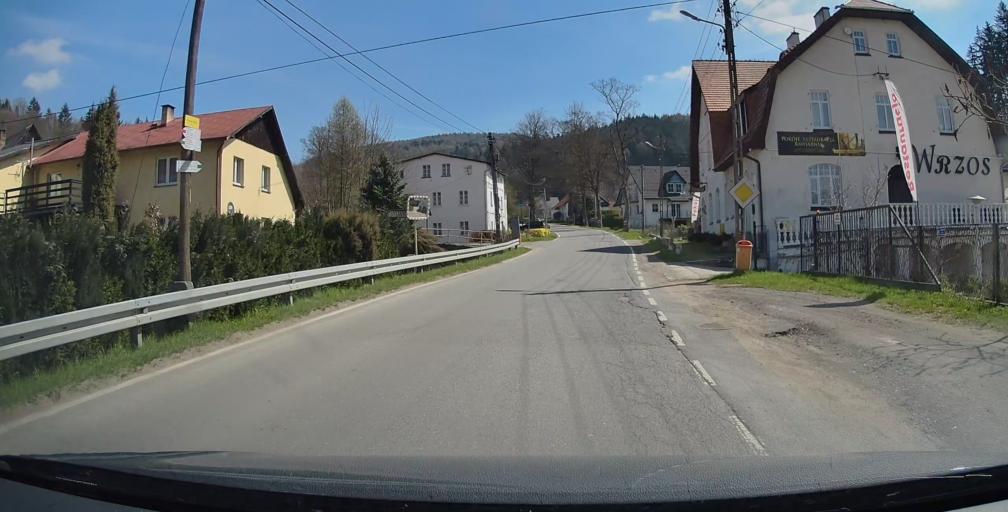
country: PL
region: Lower Silesian Voivodeship
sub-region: Powiat klodzki
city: Kudowa-Zdroj
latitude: 50.4467
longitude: 16.2647
